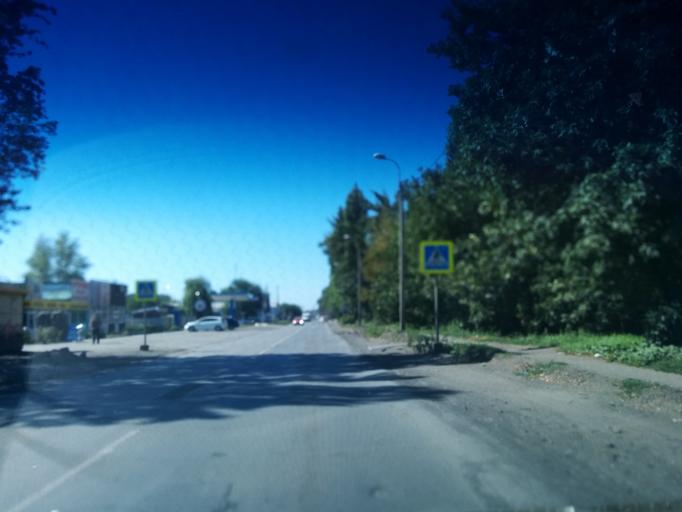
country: RU
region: Rostov
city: Shakhty
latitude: 47.6853
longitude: 40.2709
